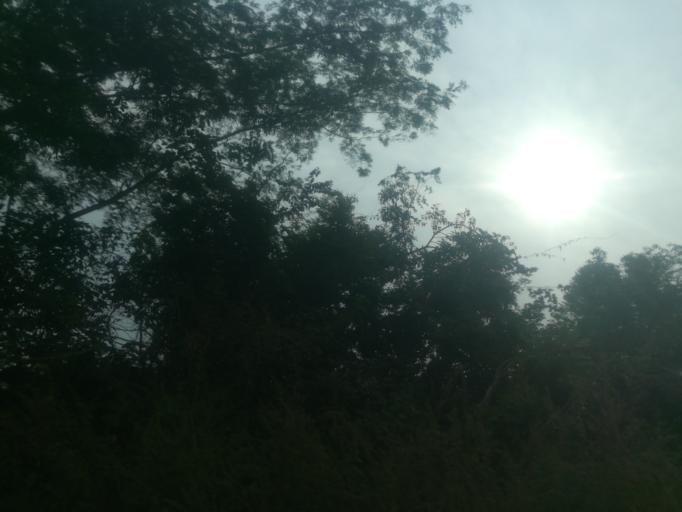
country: NG
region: Ogun
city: Ayetoro
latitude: 7.2688
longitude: 3.1052
